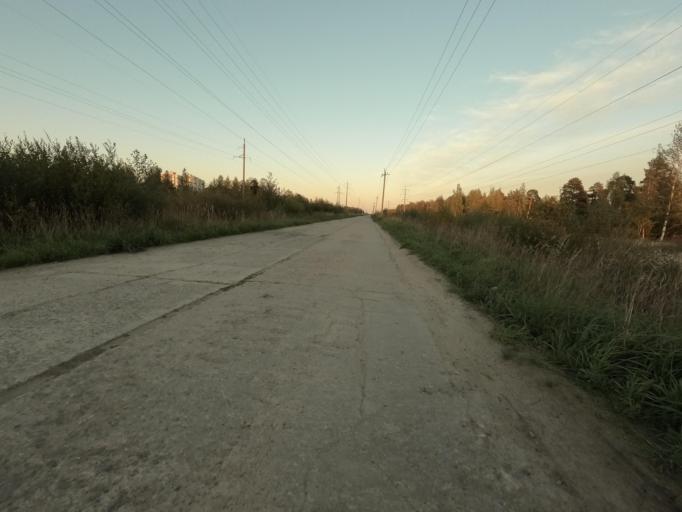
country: RU
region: Leningrad
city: Otradnoye
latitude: 59.7617
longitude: 30.7972
